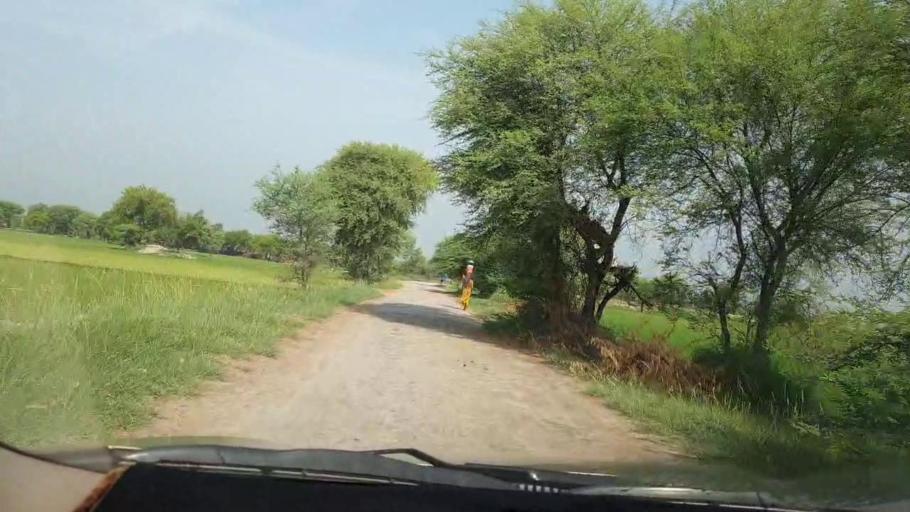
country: PK
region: Sindh
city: Goth Garelo
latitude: 27.4507
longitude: 68.0212
